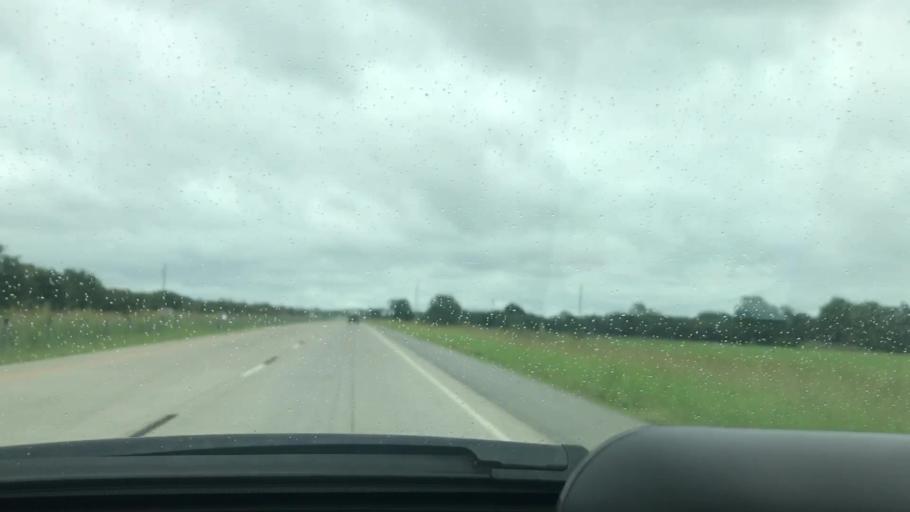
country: US
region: Oklahoma
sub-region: Pittsburg County
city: McAlester
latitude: 34.8096
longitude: -95.8605
